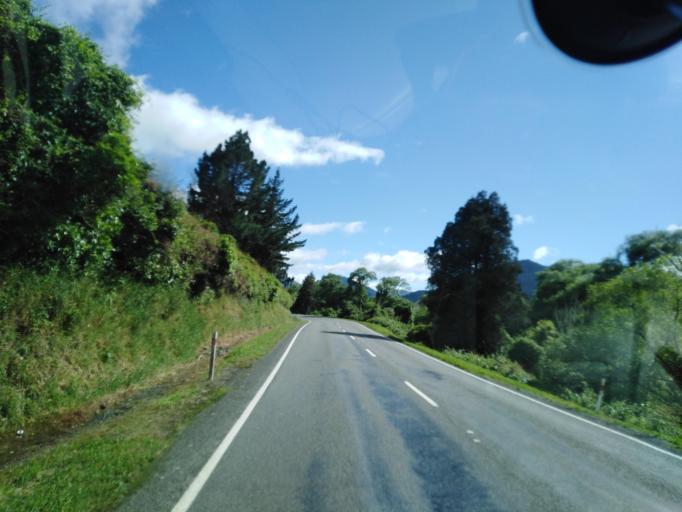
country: NZ
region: Nelson
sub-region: Nelson City
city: Nelson
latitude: -41.2545
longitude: 173.5769
